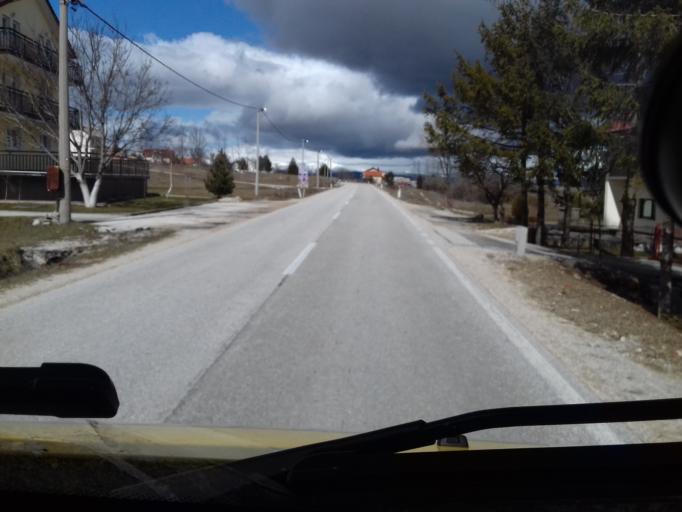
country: BA
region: Federation of Bosnia and Herzegovina
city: Dreznica
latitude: 43.6067
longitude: 17.2712
